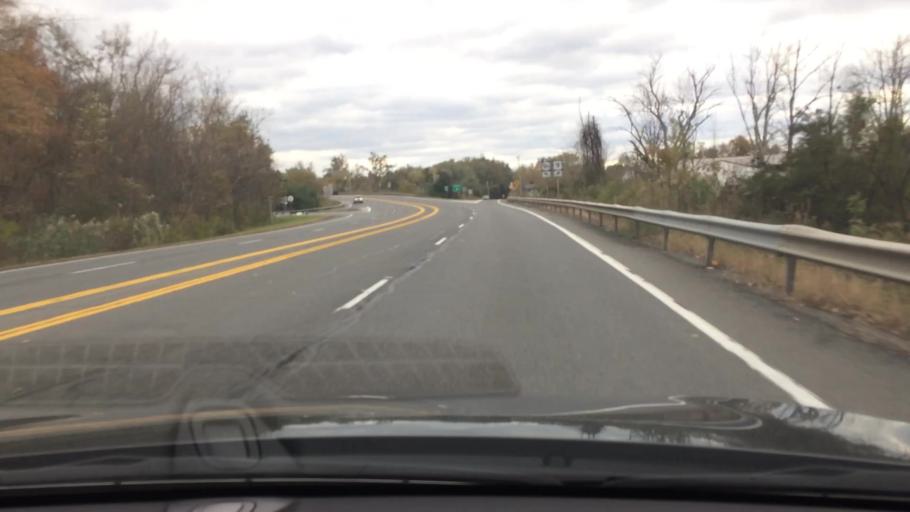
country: US
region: New York
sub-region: Columbia County
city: Kinderhook
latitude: 42.4105
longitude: -73.6913
